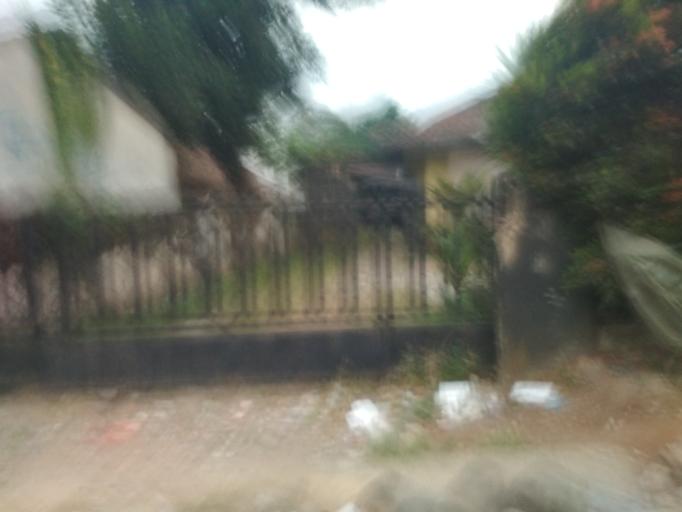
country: ID
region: West Java
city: Caringin
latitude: -6.7074
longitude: 106.8222
